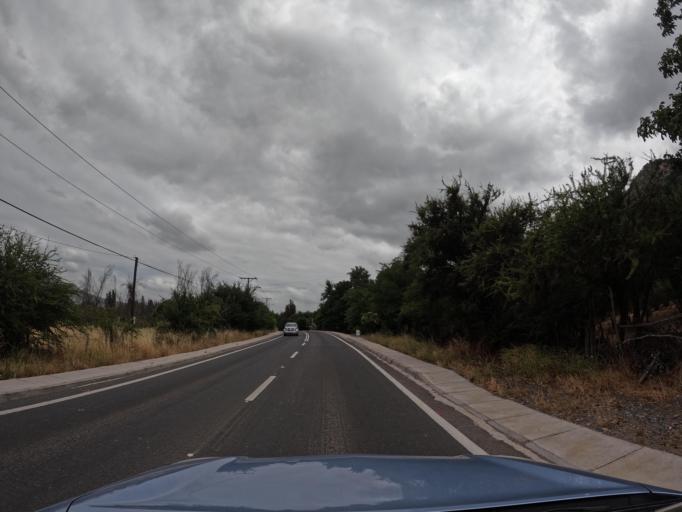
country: CL
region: Maule
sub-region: Provincia de Curico
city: Teno
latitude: -34.8130
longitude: -71.2132
